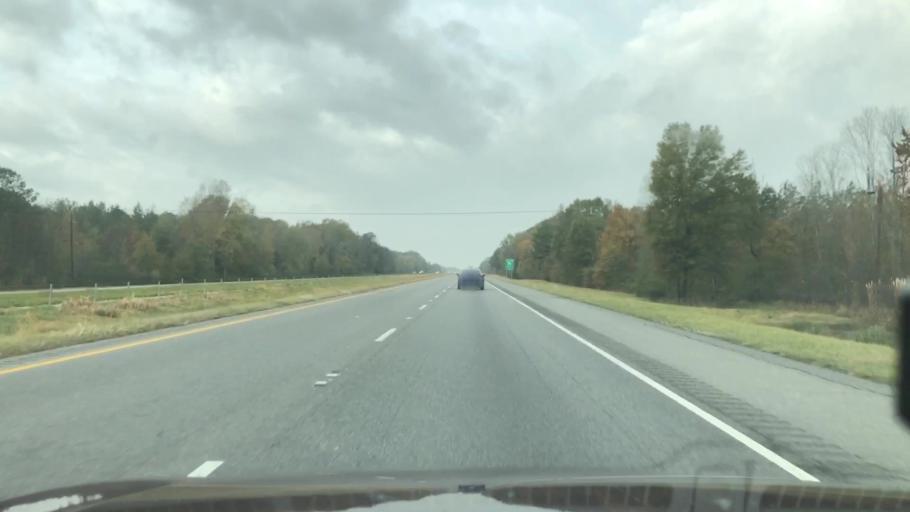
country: US
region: Louisiana
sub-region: Richland Parish
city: Delhi
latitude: 32.4478
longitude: -91.5569
